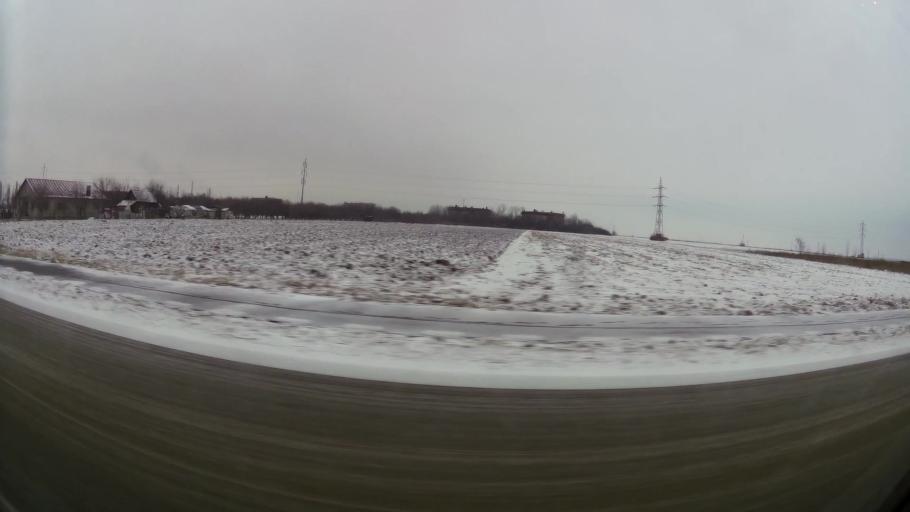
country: RO
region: Prahova
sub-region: Comuna Berceni
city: Corlatesti
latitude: 44.9286
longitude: 26.0674
